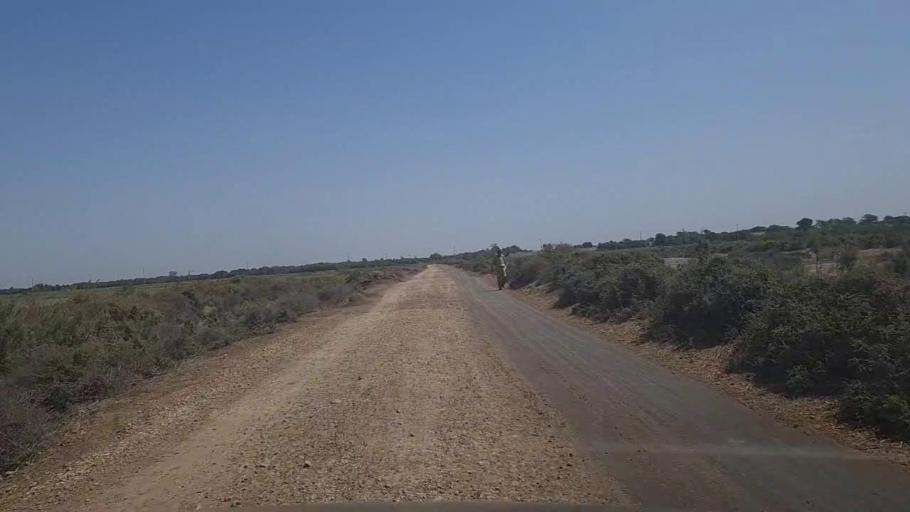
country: PK
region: Sindh
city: Thatta
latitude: 24.7857
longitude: 68.0008
